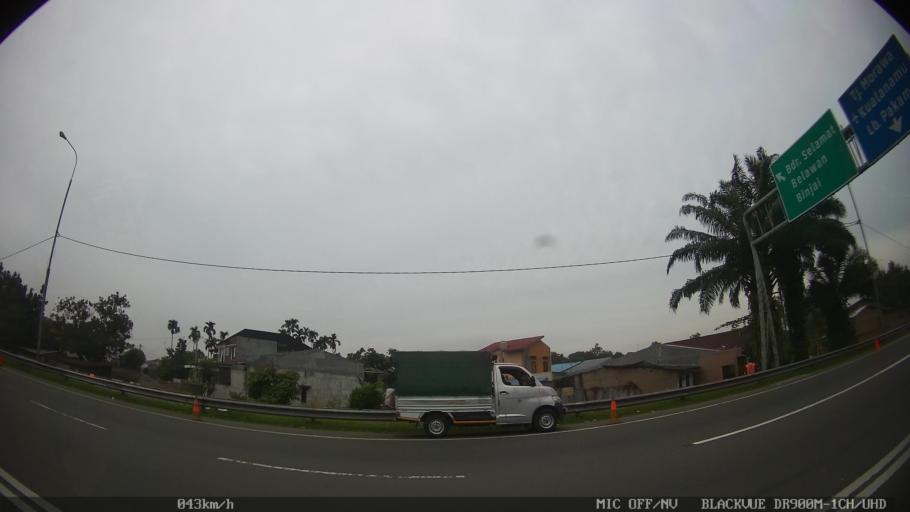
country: ID
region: North Sumatra
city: Deli Tua
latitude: 3.5418
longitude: 98.7250
